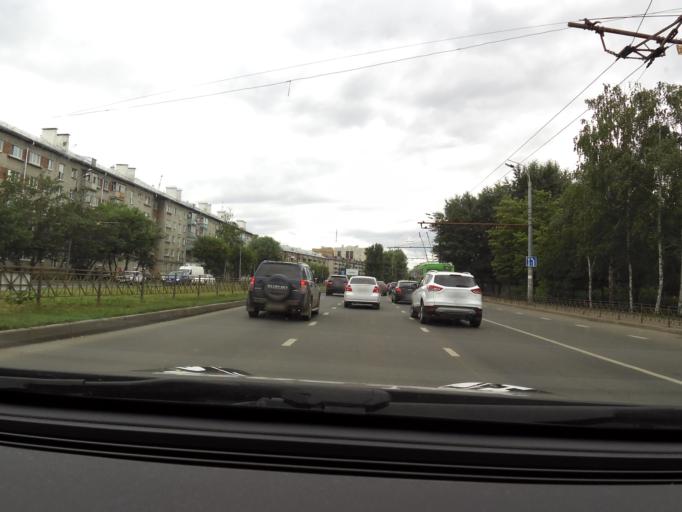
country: RU
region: Tatarstan
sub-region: Gorod Kazan'
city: Kazan
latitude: 55.8185
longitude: 49.0577
